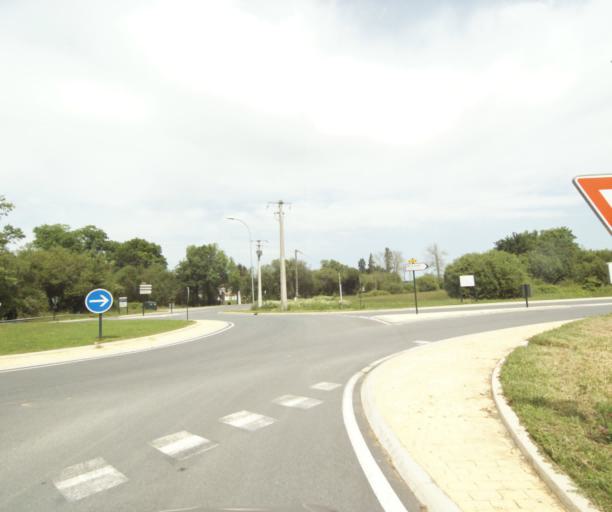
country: FR
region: Aquitaine
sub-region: Departement des Pyrenees-Atlantiques
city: Mouguerre
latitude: 43.4923
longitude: -1.4243
